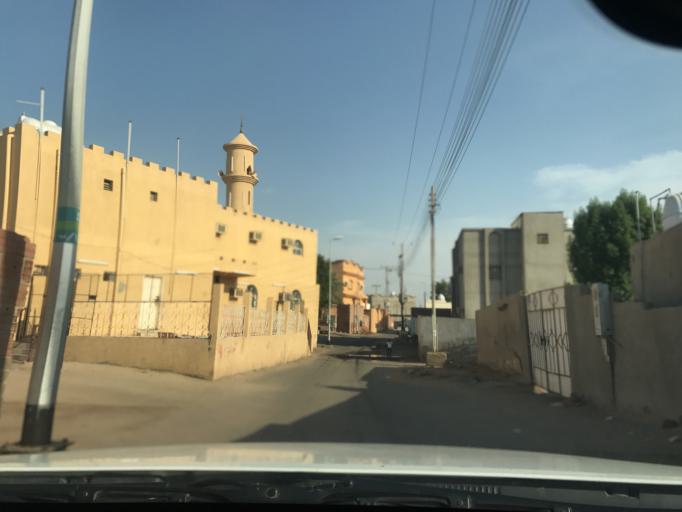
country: SA
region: Makkah
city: Al Jumum
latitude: 21.4452
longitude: 39.5340
